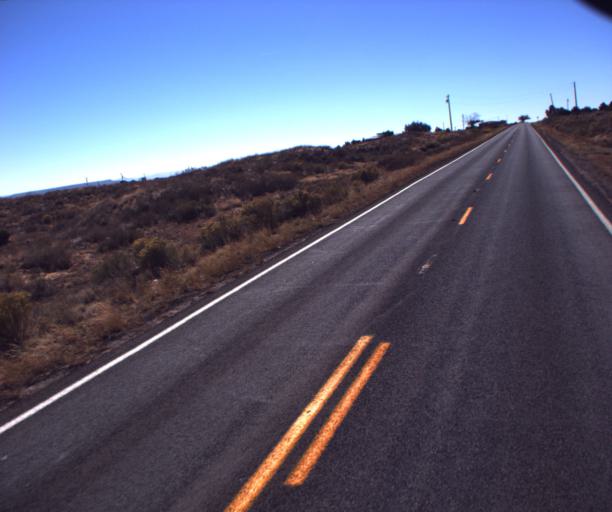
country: US
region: Arizona
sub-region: Navajo County
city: First Mesa
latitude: 35.9162
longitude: -110.6639
